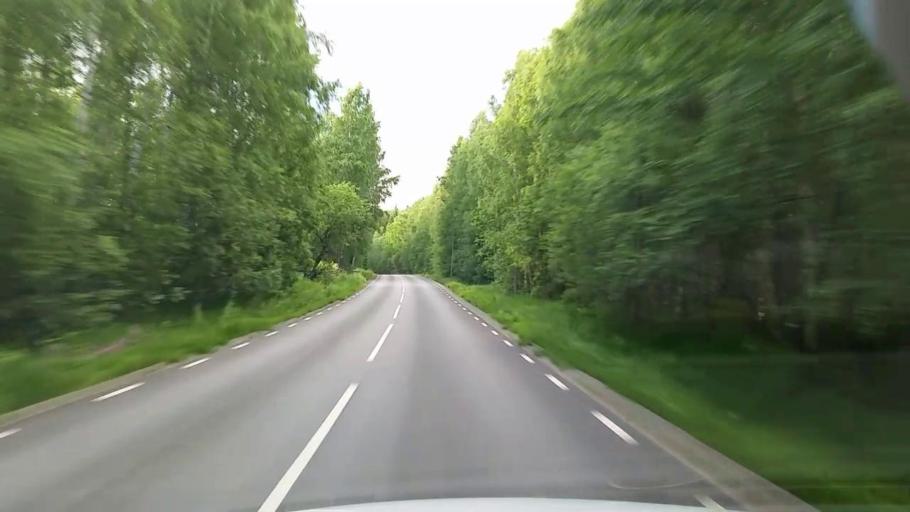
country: SE
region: Vaestmanland
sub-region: Kopings Kommun
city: Kolsva
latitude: 59.7222
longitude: 15.8331
